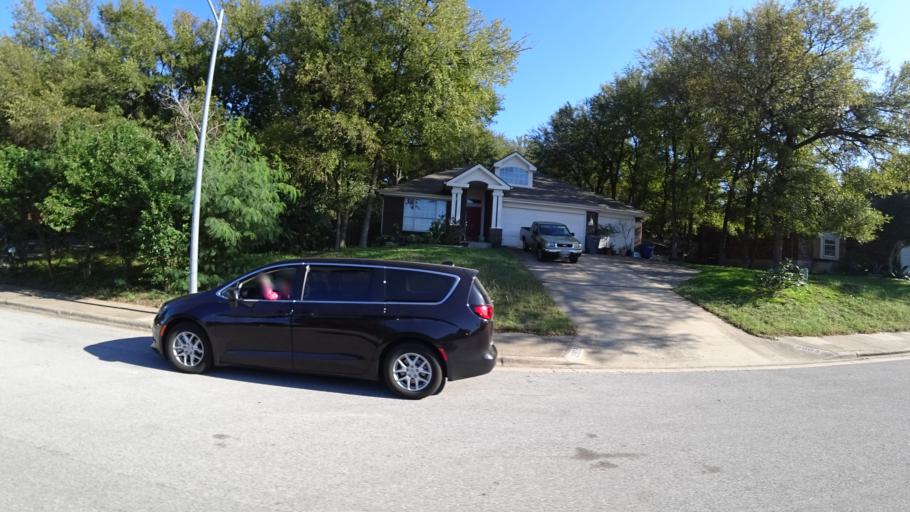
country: US
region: Texas
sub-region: Travis County
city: Austin
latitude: 30.2209
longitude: -97.7257
